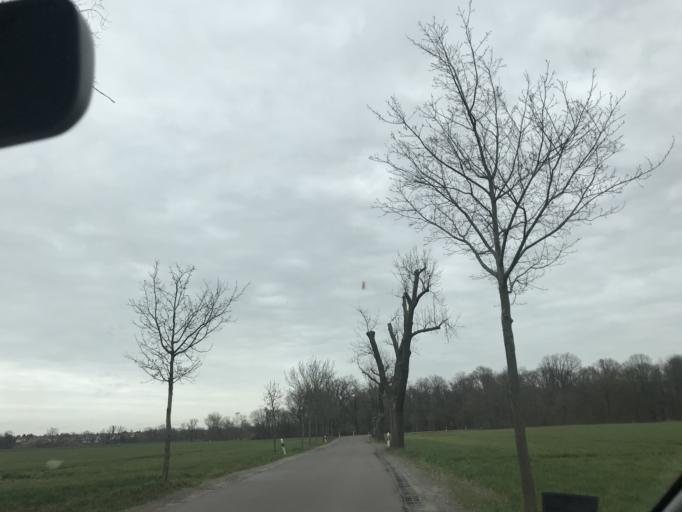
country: DE
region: Saxony
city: Schkeuditz
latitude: 51.3754
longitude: 12.2624
